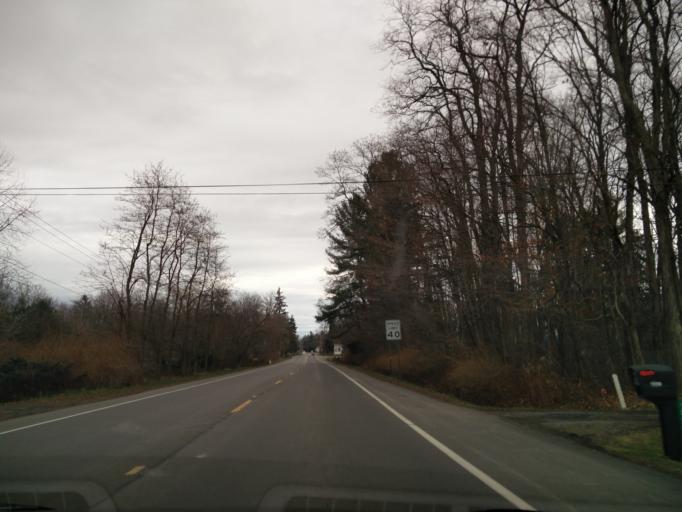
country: US
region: New York
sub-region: Tompkins County
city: Trumansburg
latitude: 42.5119
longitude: -76.6189
